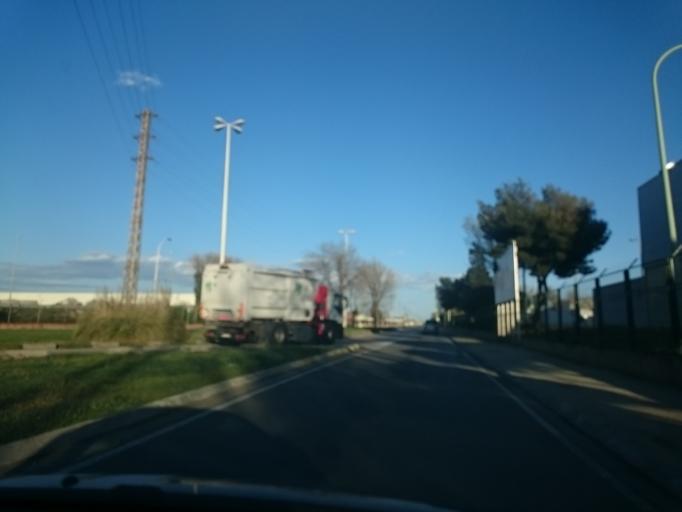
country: ES
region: Catalonia
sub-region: Provincia de Barcelona
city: El Prat de Llobregat
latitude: 41.3363
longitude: 2.1135
